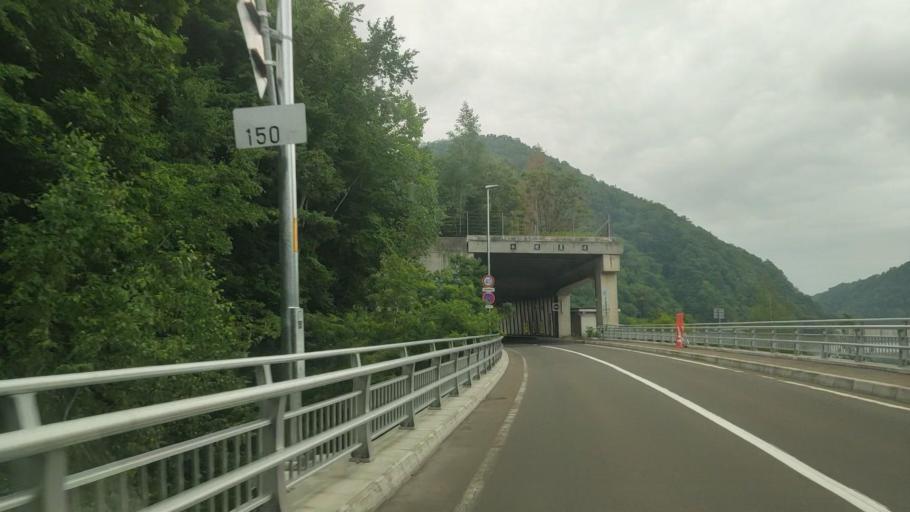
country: JP
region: Hokkaido
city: Sapporo
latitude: 42.9921
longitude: 141.1604
